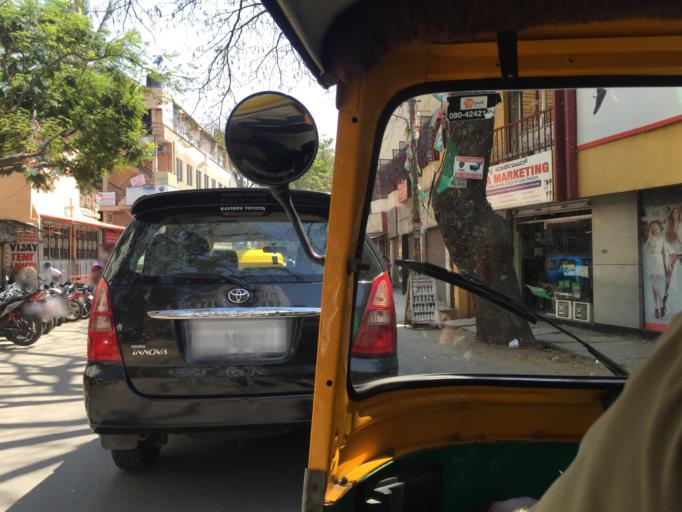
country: IN
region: Karnataka
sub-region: Bangalore Urban
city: Bangalore
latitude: 12.9731
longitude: 77.6470
